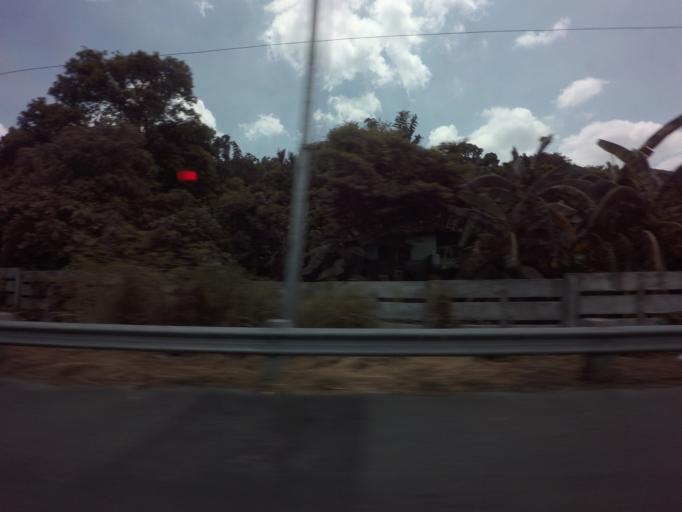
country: PH
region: Calabarzon
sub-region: Province of Laguna
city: San Pedro
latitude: 14.3783
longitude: 121.0308
